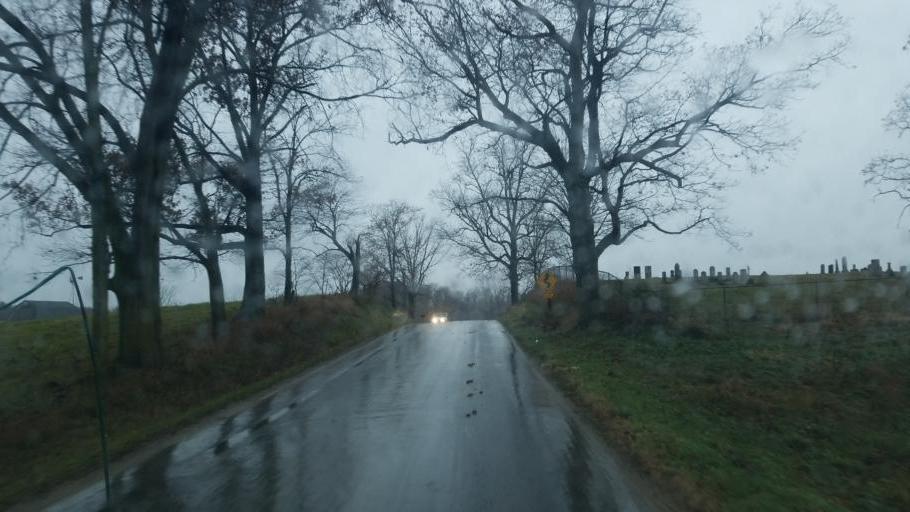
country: US
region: Indiana
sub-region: Adams County
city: Geneva
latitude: 40.6146
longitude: -84.9305
